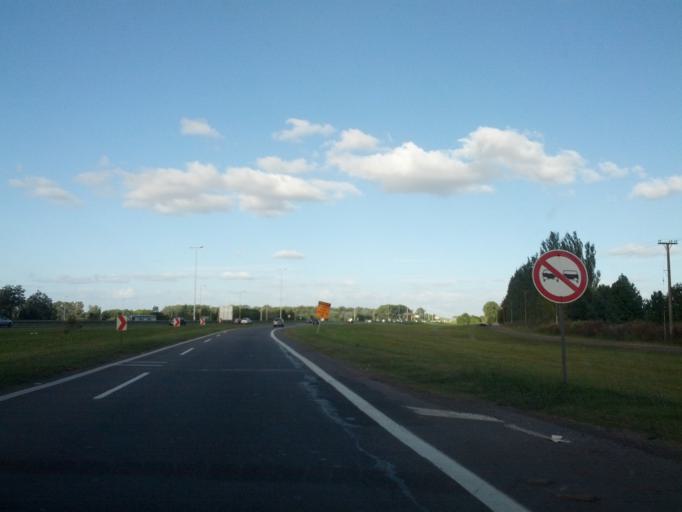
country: AR
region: Buenos Aires
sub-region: Partido de Lujan
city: Lujan
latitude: -34.5692
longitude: -59.0608
